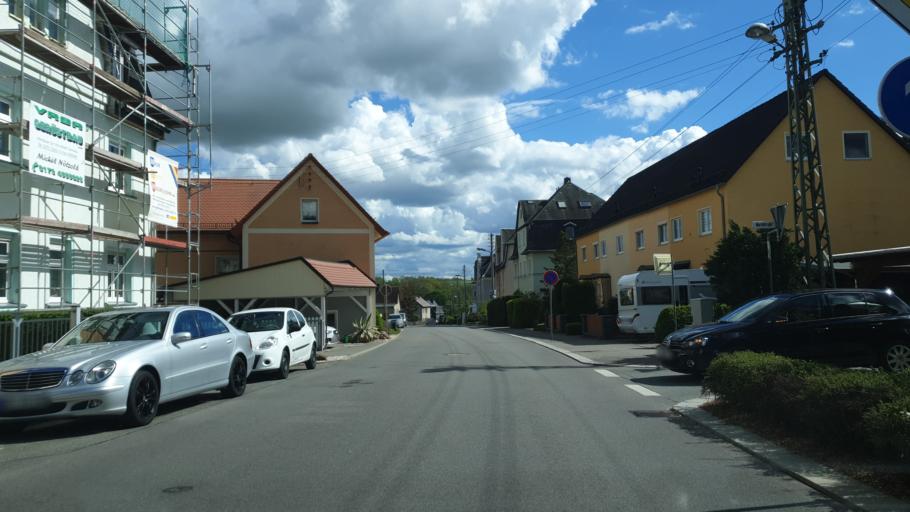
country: DE
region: Saxony
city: Kirchberg
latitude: 50.7942
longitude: 12.7455
